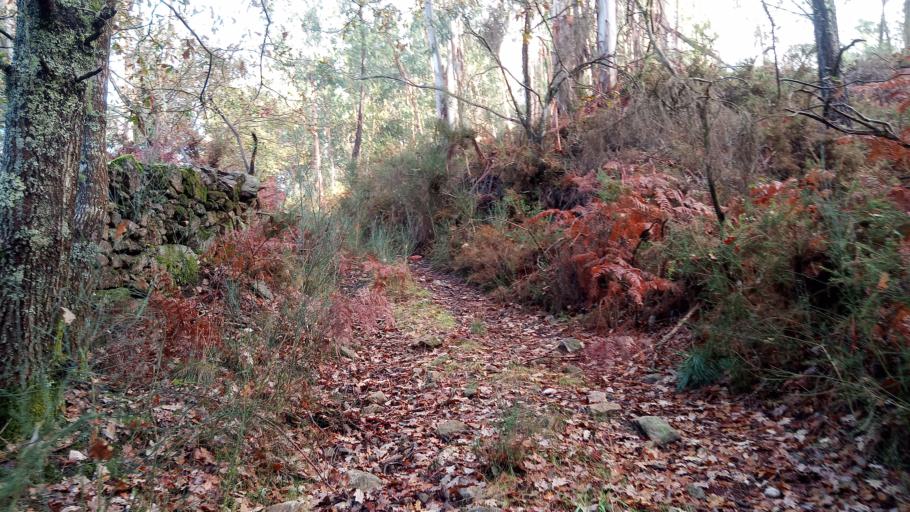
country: PT
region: Viana do Castelo
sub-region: Paredes de Coura
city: Paredes de Coura
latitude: 41.8950
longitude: -8.6131
